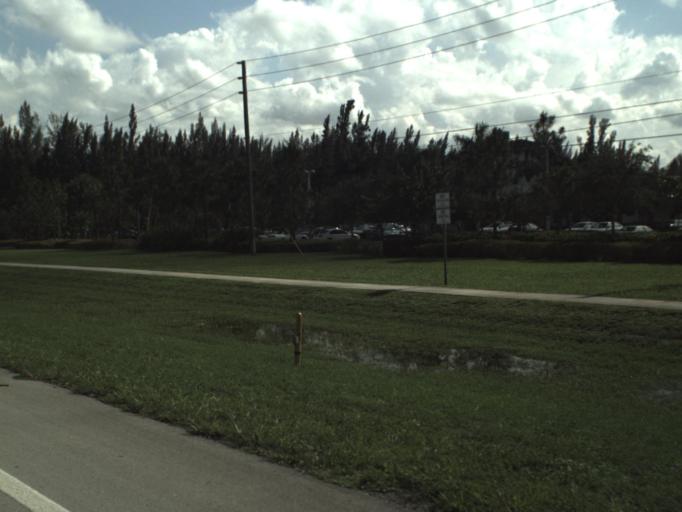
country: US
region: Florida
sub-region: Palm Beach County
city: Kings Point
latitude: 26.3996
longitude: -80.2039
